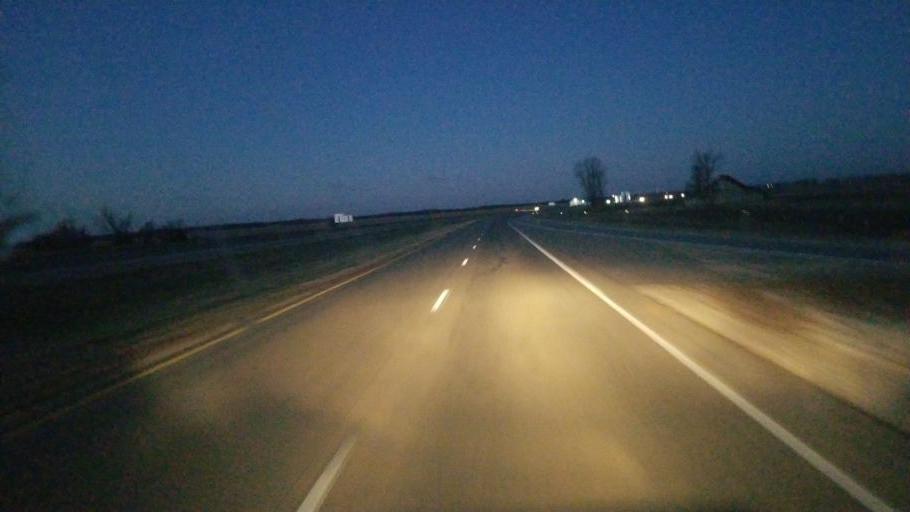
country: US
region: Iowa
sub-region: Des Moines County
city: West Burlington
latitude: 40.8299
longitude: -91.2735
